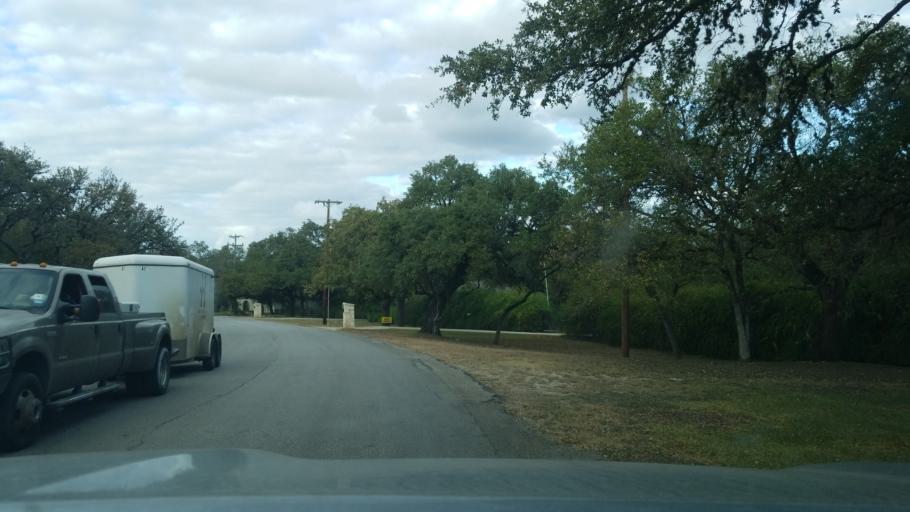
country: US
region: Texas
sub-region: Bexar County
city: Hollywood Park
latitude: 29.5960
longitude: -98.4785
